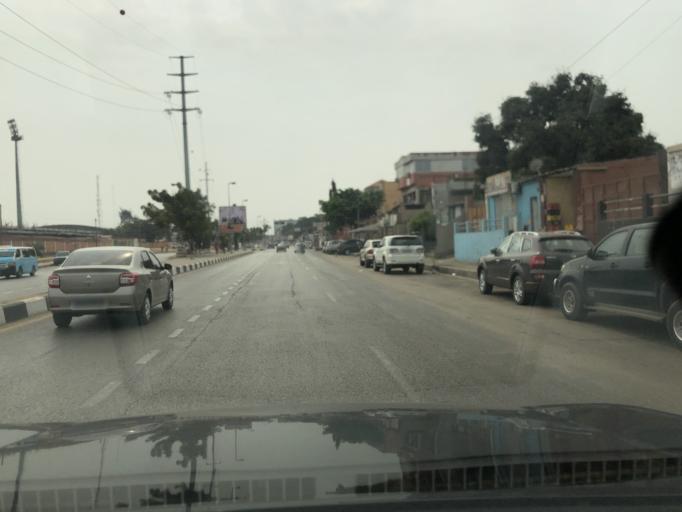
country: AO
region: Luanda
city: Luanda
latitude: -8.8427
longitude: 13.2388
